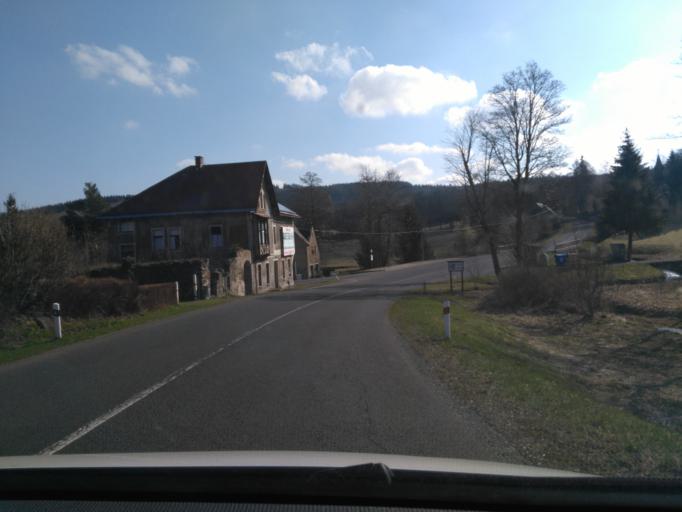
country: DE
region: Saxony
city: Johstadt
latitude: 50.4897
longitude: 13.0770
